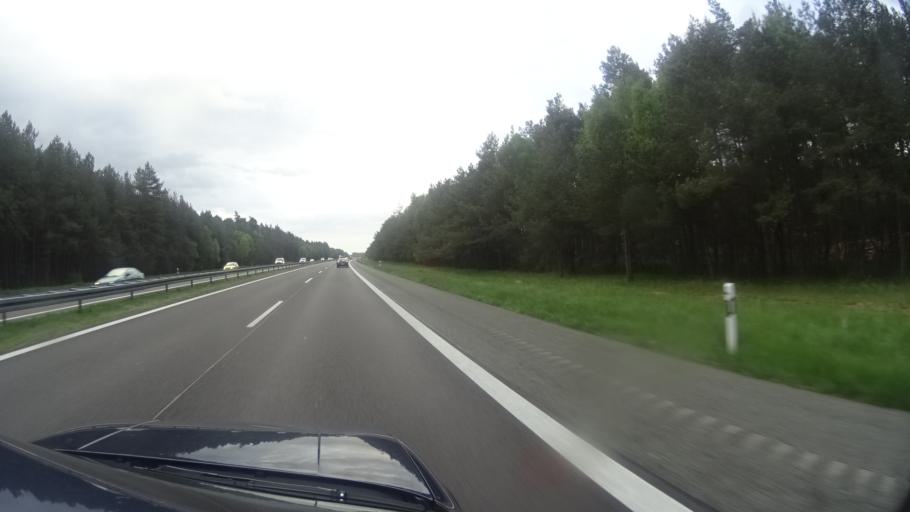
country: DE
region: Brandenburg
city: Walsleben
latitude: 53.0315
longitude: 12.5679
